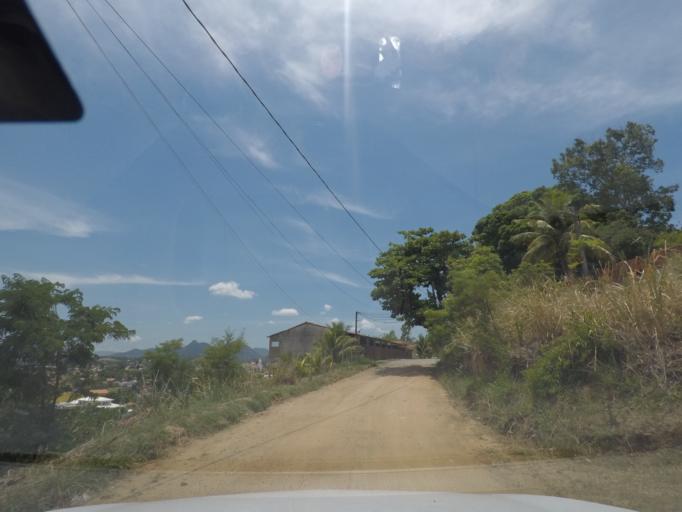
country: BR
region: Rio de Janeiro
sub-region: Marica
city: Marica
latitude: -22.9247
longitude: -42.8271
